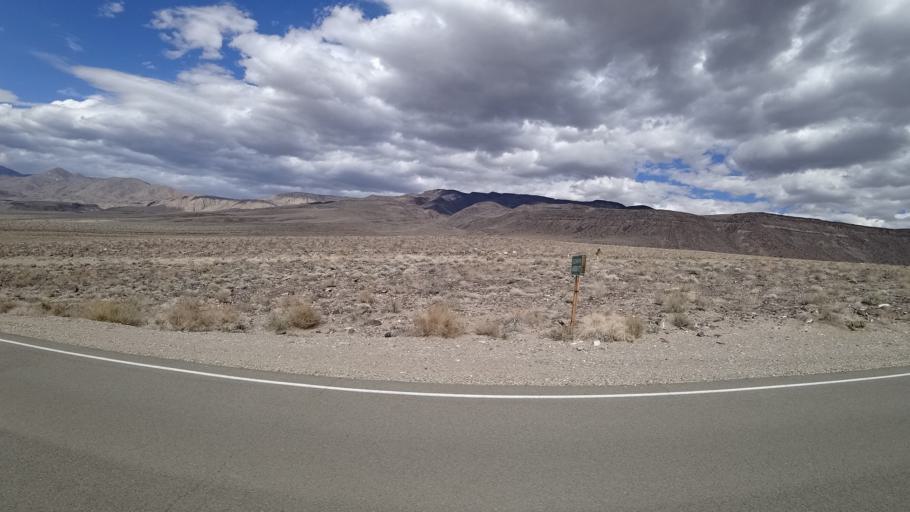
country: US
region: California
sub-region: Inyo County
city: Lone Pine
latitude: 36.4142
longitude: -117.8134
